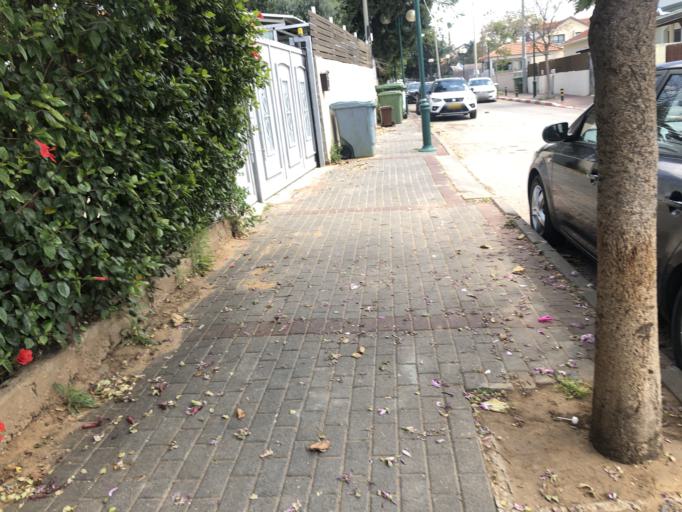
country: IL
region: Central District
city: Hod HaSharon
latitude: 32.1524
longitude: 34.9121
